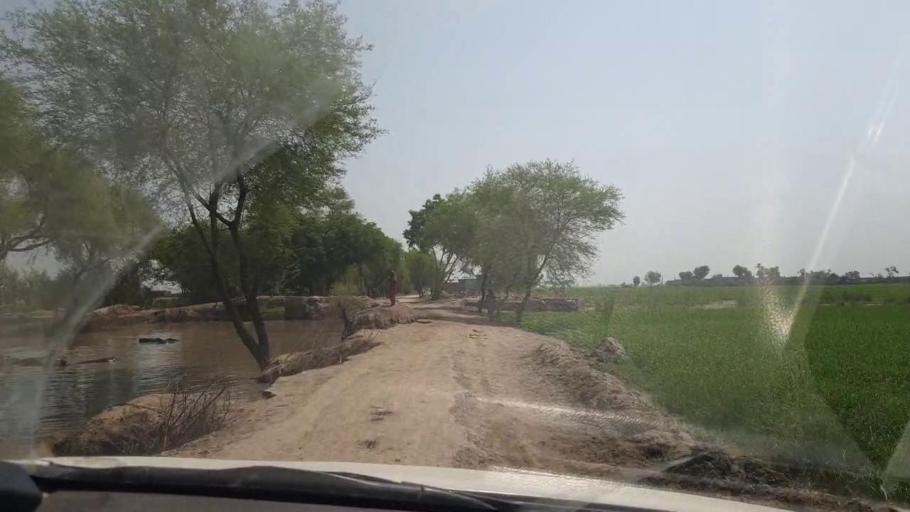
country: PK
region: Sindh
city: Chak
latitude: 27.8926
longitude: 68.7929
